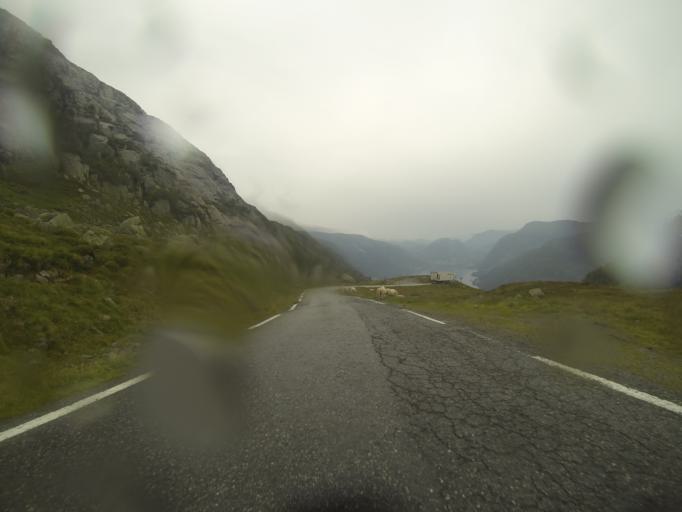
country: NO
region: Hordaland
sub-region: Odda
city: Odda
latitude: 59.7810
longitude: 6.7530
